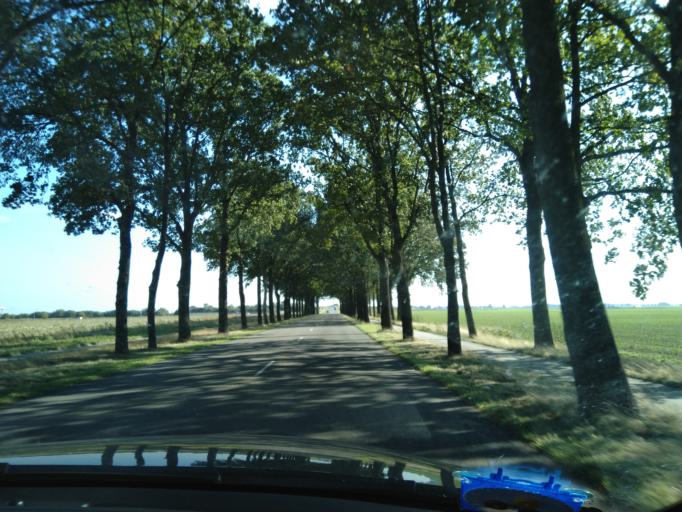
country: NL
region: Groningen
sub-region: Gemeente Veendam
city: Veendam
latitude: 53.0822
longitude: 6.8759
